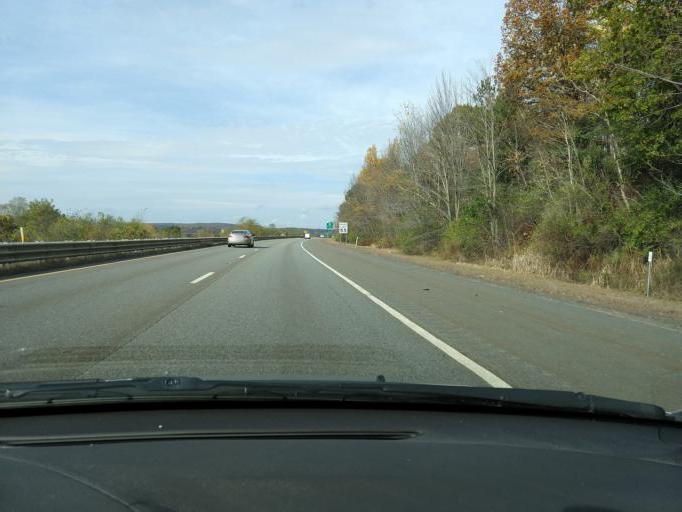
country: US
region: Massachusetts
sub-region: Worcester County
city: Leominster
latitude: 42.5239
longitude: -71.7255
